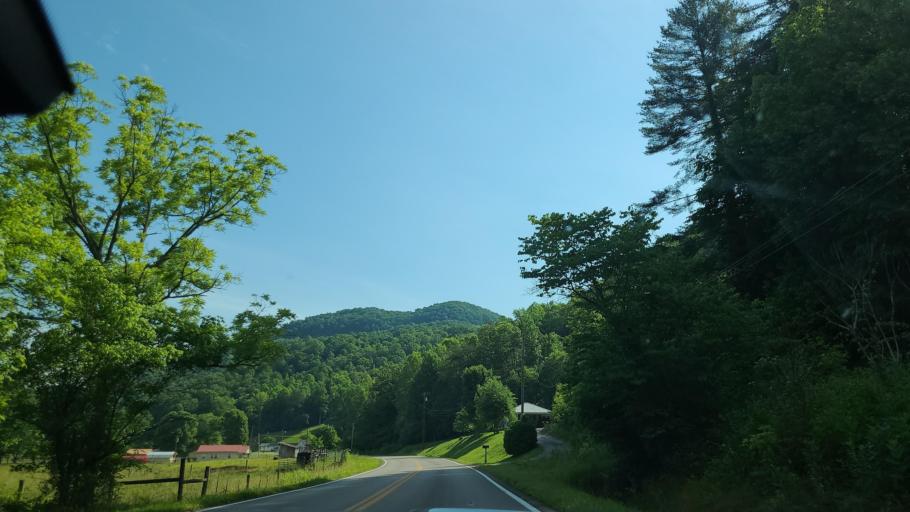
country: US
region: Kentucky
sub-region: Bell County
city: Pineville
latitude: 36.7282
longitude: -83.7993
